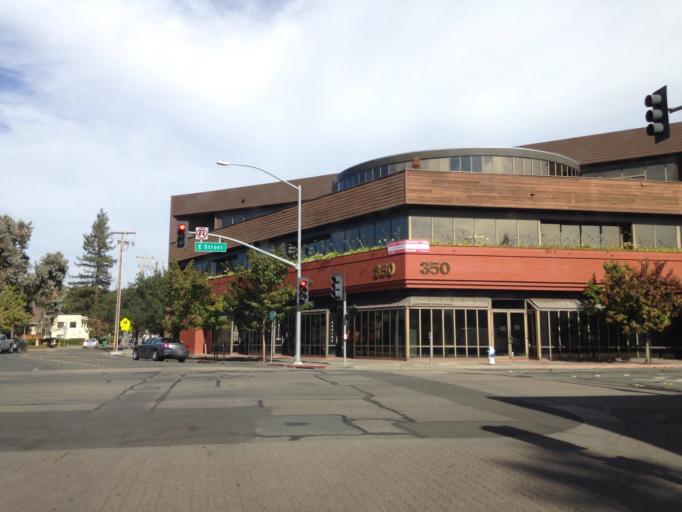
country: US
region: California
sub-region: Sonoma County
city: Santa Rosa
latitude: 38.4425
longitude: -122.7115
